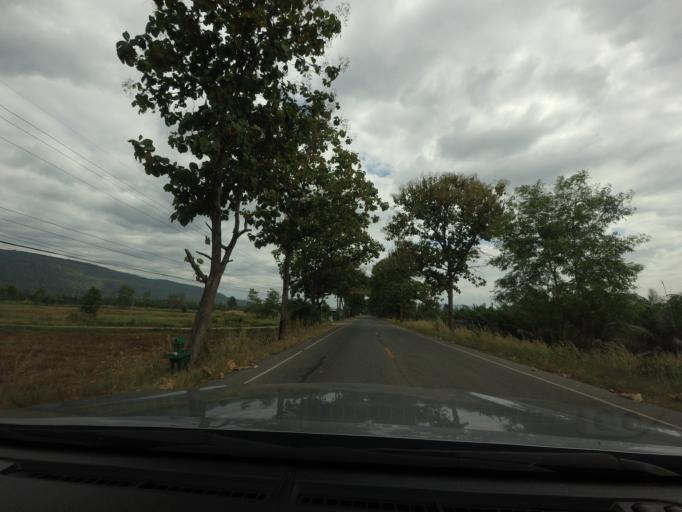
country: TH
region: Phitsanulok
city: Wang Thong
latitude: 16.7071
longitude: 100.4919
